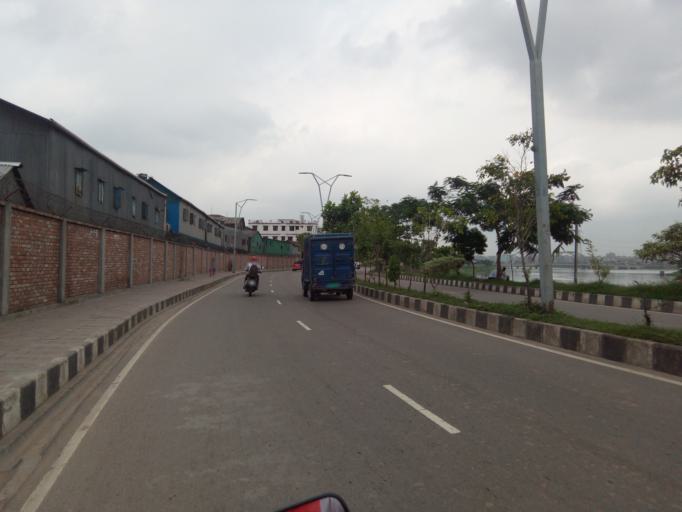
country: BD
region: Dhaka
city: Paltan
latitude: 23.7575
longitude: 90.4032
